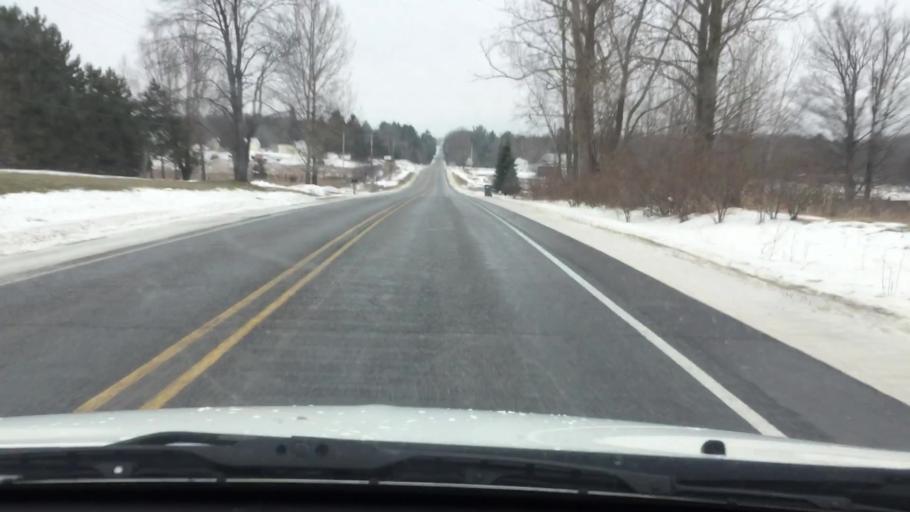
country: US
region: Michigan
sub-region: Wexford County
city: Cadillac
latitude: 44.0639
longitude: -85.4440
